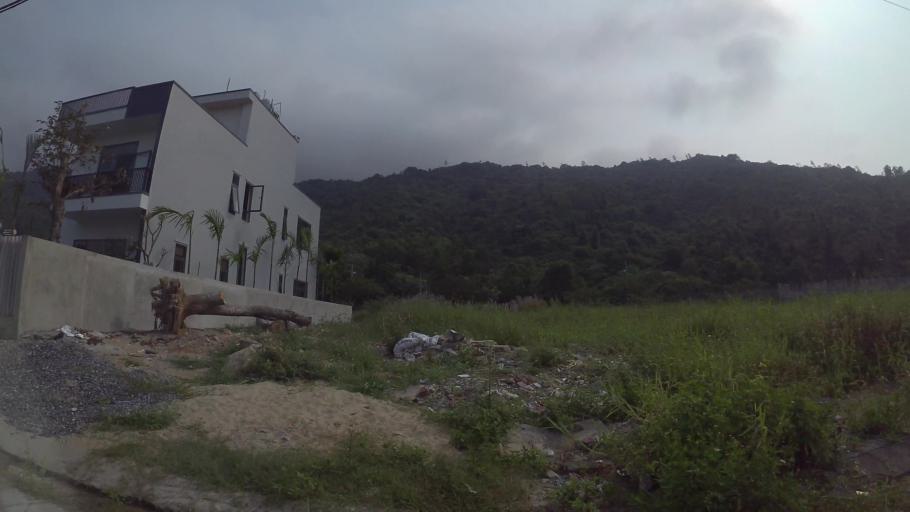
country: VN
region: Da Nang
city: Son Tra
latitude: 16.1063
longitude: 108.2625
